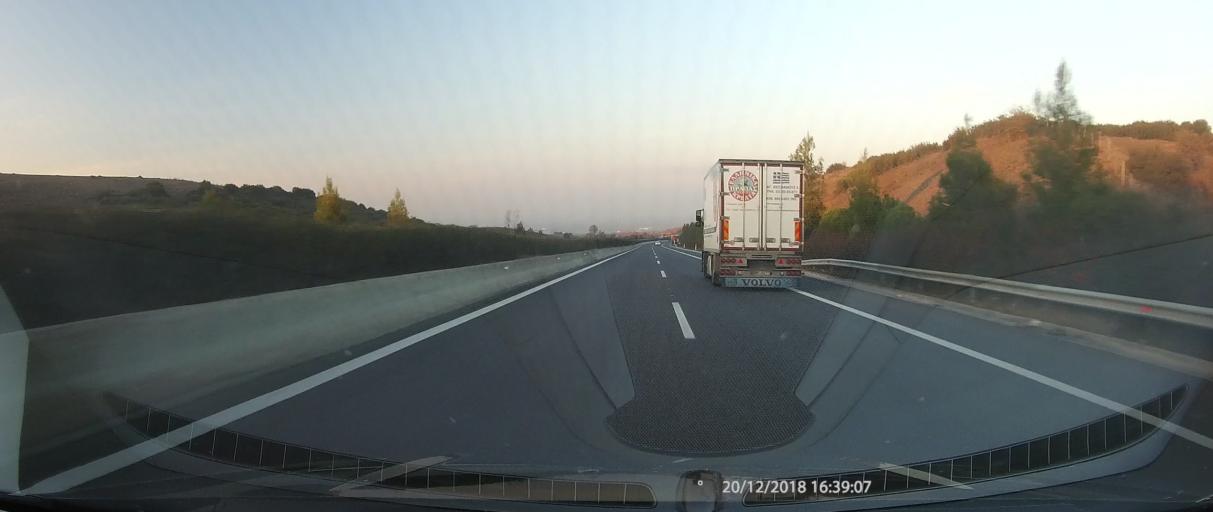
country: GR
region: Thessaly
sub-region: Nomos Magnisias
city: Velestino
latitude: 39.3525
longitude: 22.7725
